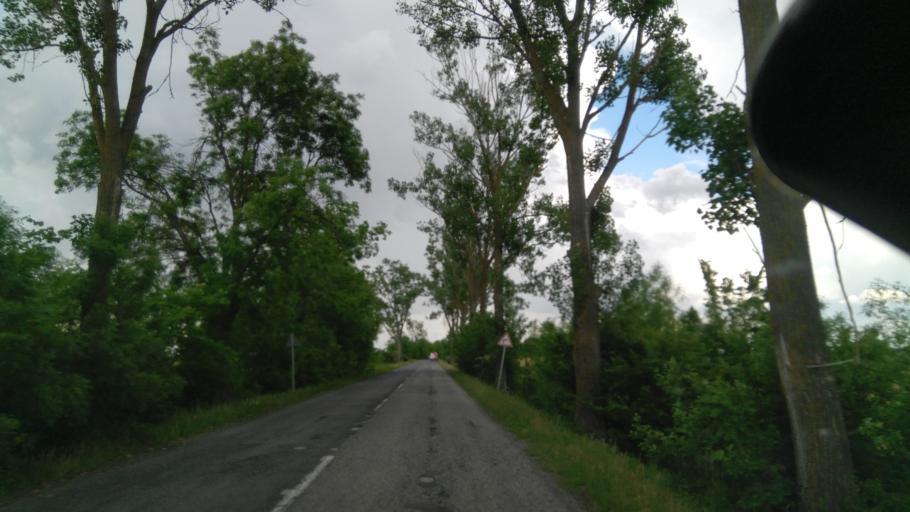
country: HU
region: Bekes
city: Fuzesgyarmat
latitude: 47.1496
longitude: 21.1298
